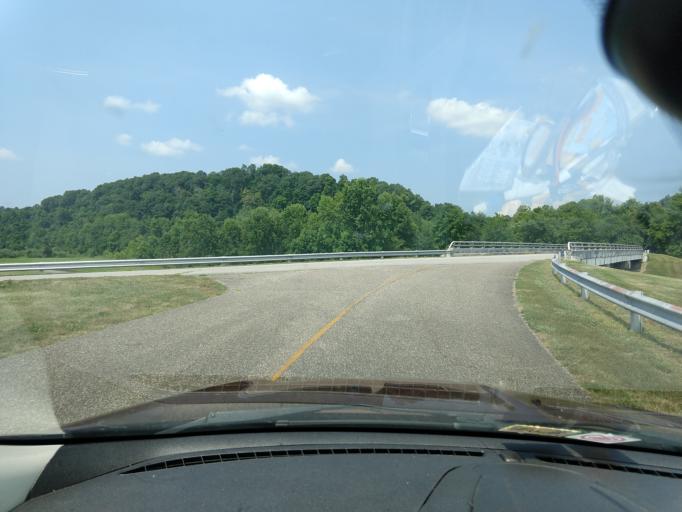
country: US
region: West Virginia
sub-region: Mason County
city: New Haven
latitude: 38.9222
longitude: -81.9110
